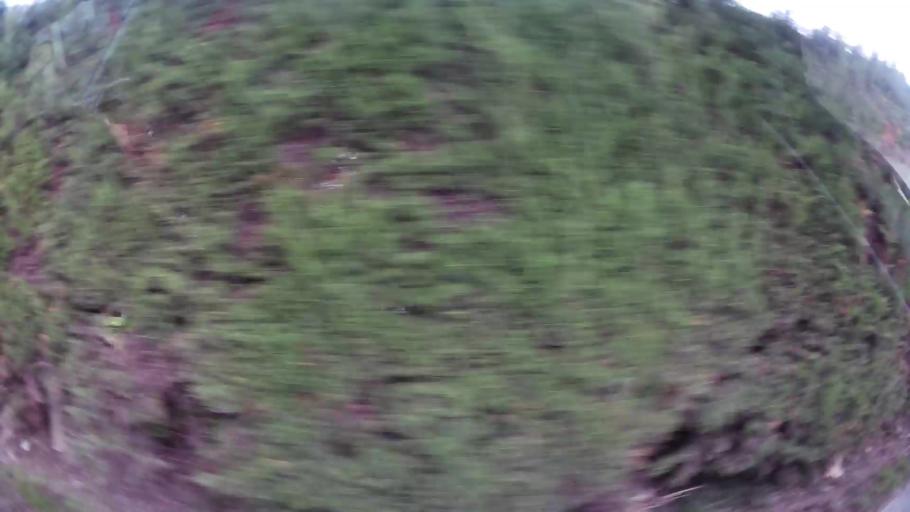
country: CO
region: Cundinamarca
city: Cota
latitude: 4.8161
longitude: -74.1064
